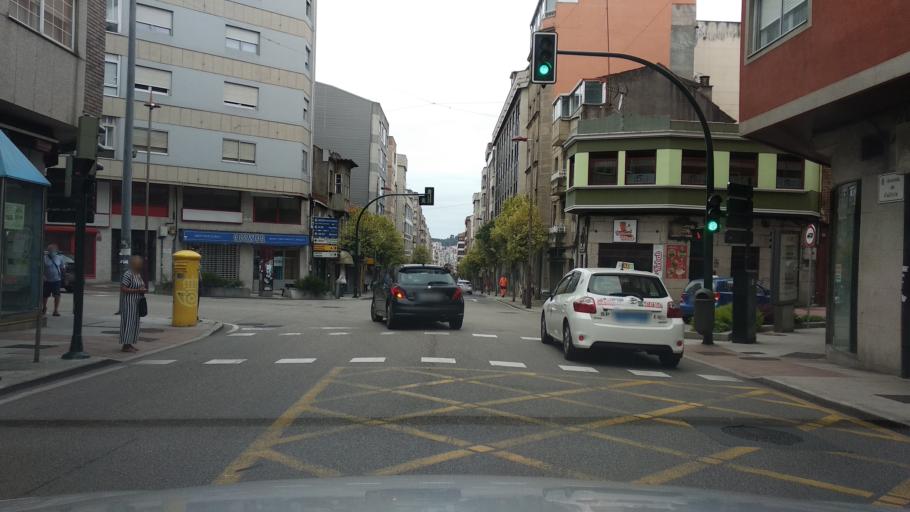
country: ES
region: Galicia
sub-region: Provincia de Pontevedra
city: Vigo
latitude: 42.2502
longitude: -8.6955
